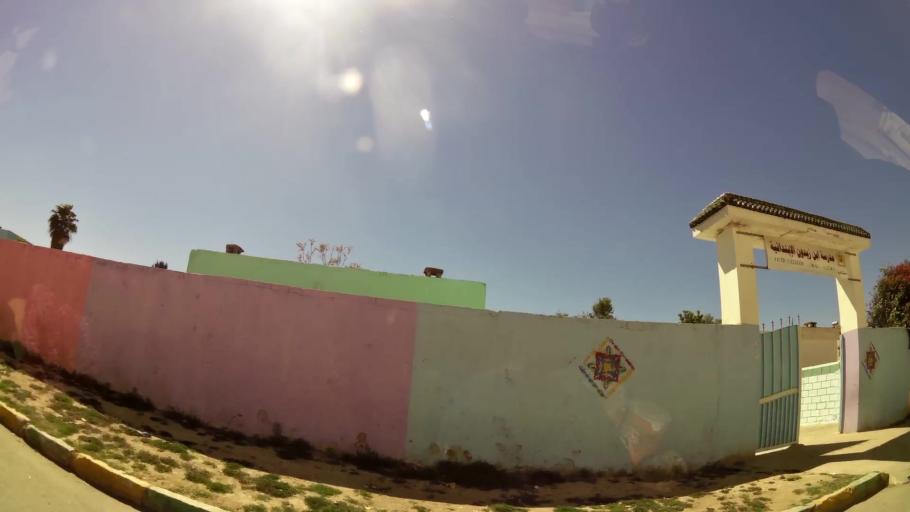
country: MA
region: Meknes-Tafilalet
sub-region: Meknes
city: Meknes
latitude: 33.8890
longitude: -5.5731
